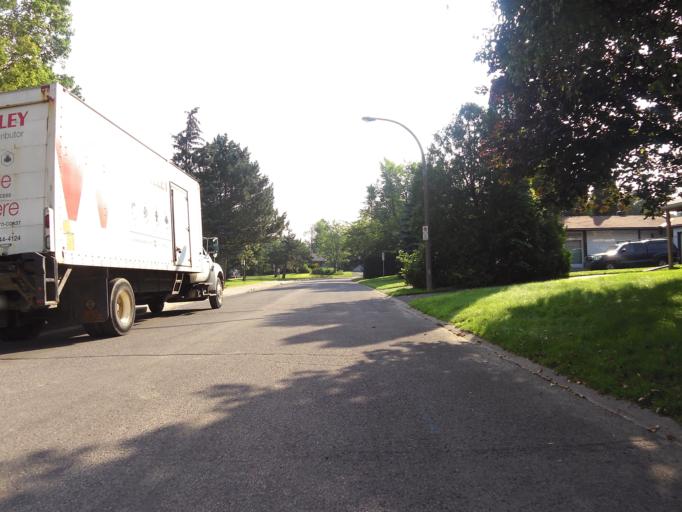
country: CA
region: Ontario
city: Bells Corners
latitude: 45.3370
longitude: -75.7774
